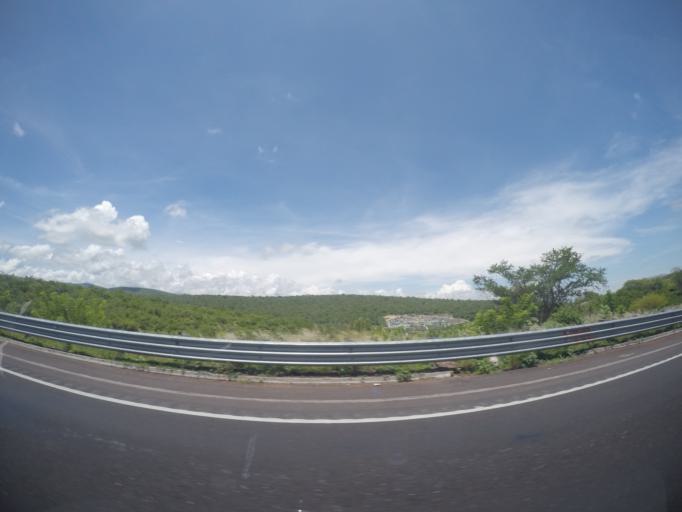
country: MX
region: Morelos
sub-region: Jojutla
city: Higueron
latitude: 18.5554
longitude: -99.2101
